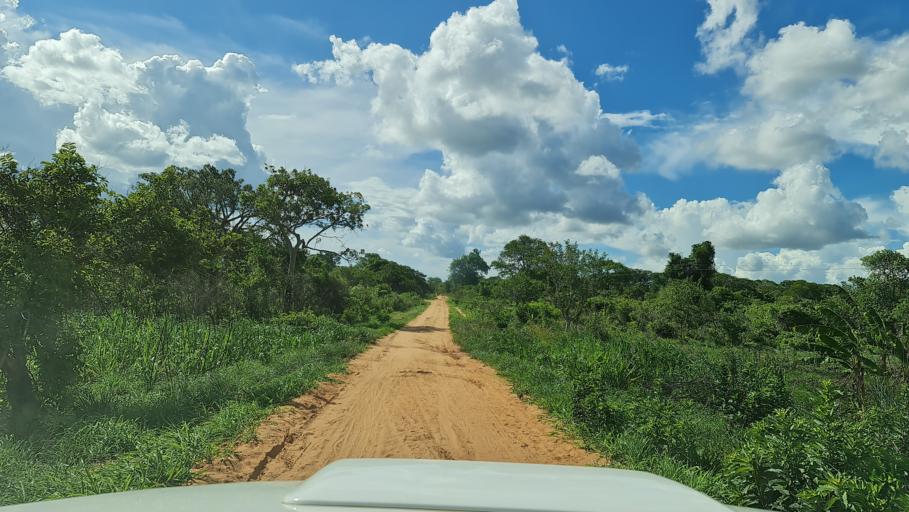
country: MZ
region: Nampula
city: Ilha de Mocambique
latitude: -15.4161
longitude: 40.2591
